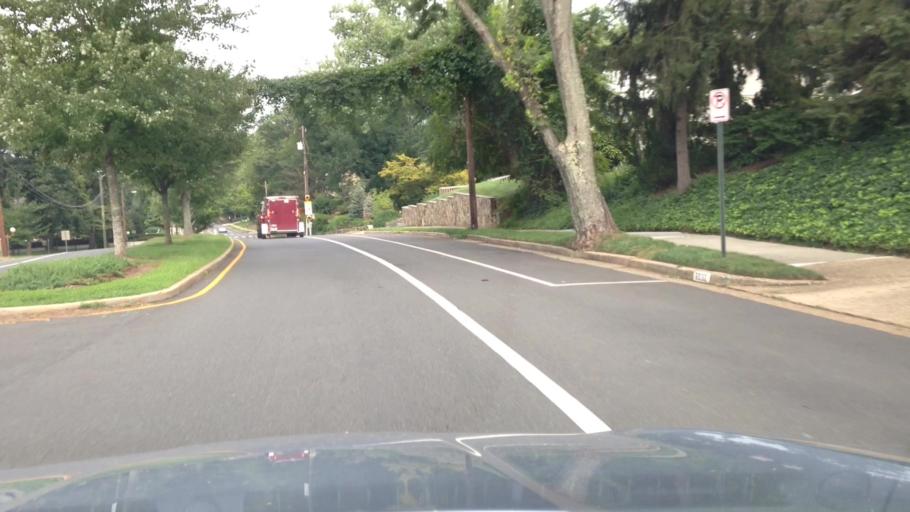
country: US
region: Virginia
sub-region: City of Falls Church
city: Falls Church
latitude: 38.9007
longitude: -77.1543
